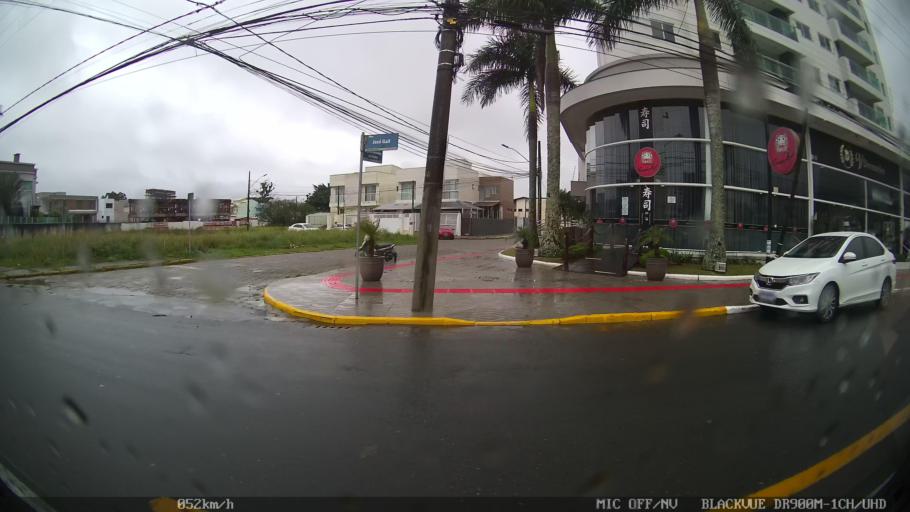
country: BR
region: Santa Catarina
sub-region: Itajai
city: Itajai
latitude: -26.9227
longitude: -48.6800
